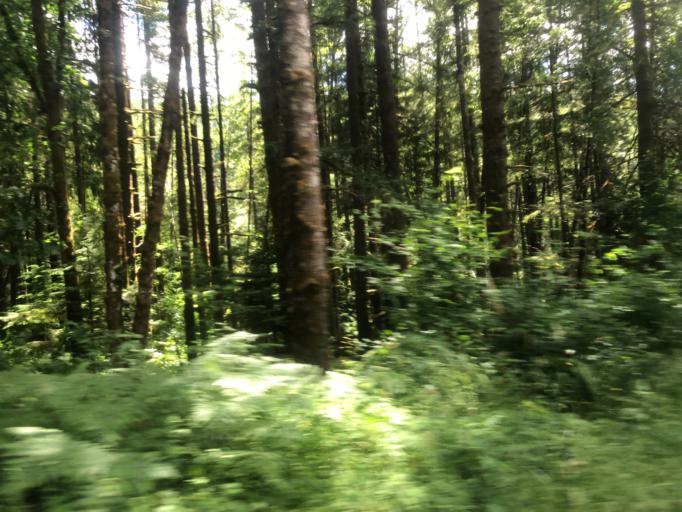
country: US
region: Oregon
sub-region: Clackamas County
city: Mount Hood Village
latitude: 45.4898
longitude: -122.0413
